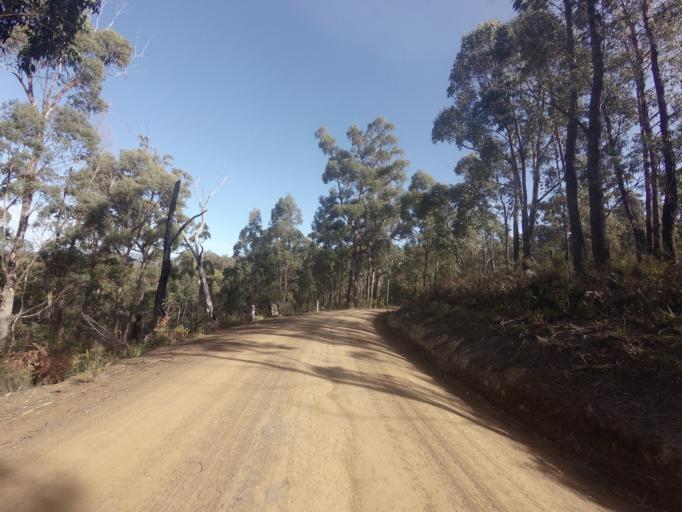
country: AU
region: Tasmania
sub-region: Kingborough
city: Kettering
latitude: -43.0949
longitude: 147.2630
